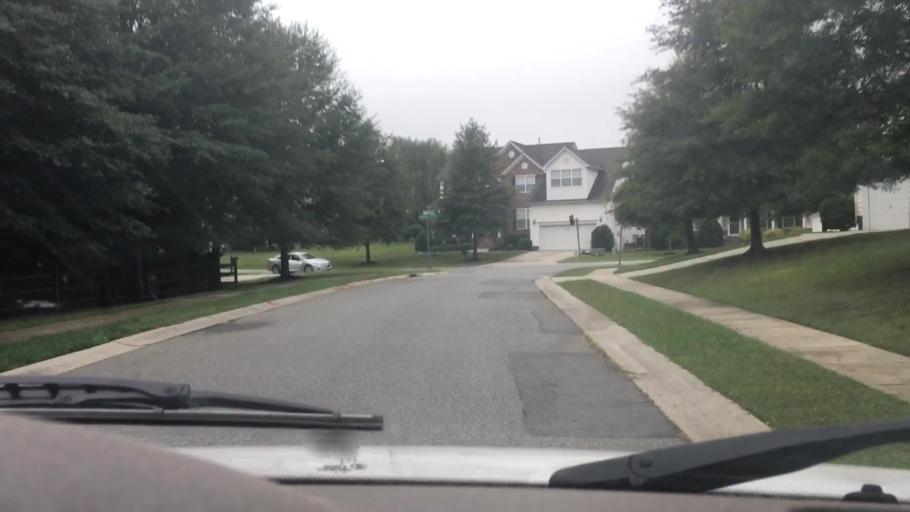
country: US
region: North Carolina
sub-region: Mecklenburg County
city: Huntersville
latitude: 35.3954
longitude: -80.7435
